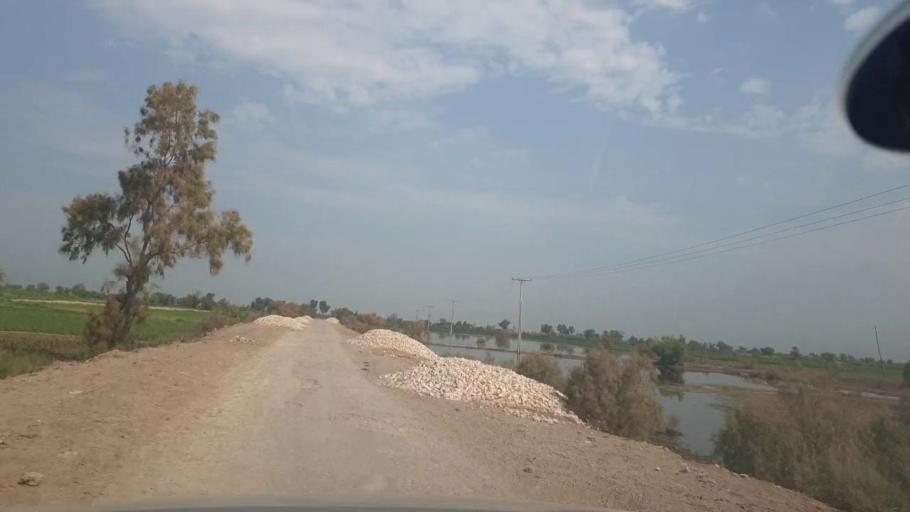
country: PK
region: Balochistan
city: Mehrabpur
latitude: 28.0686
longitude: 68.1027
